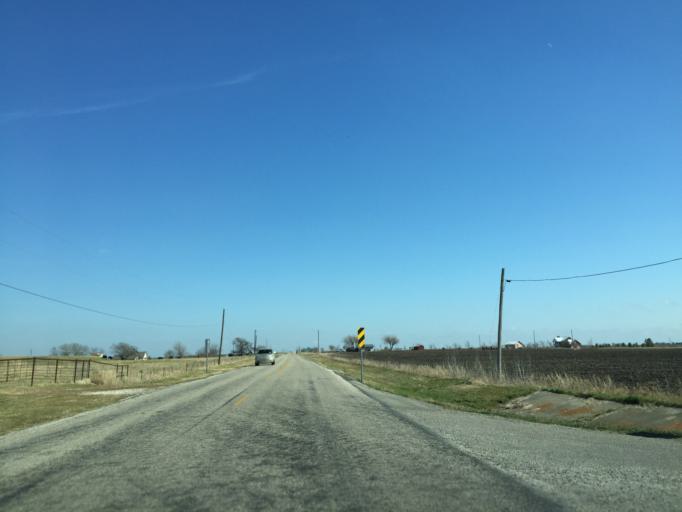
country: US
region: Texas
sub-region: Williamson County
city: Granger
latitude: 30.7524
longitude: -97.5479
